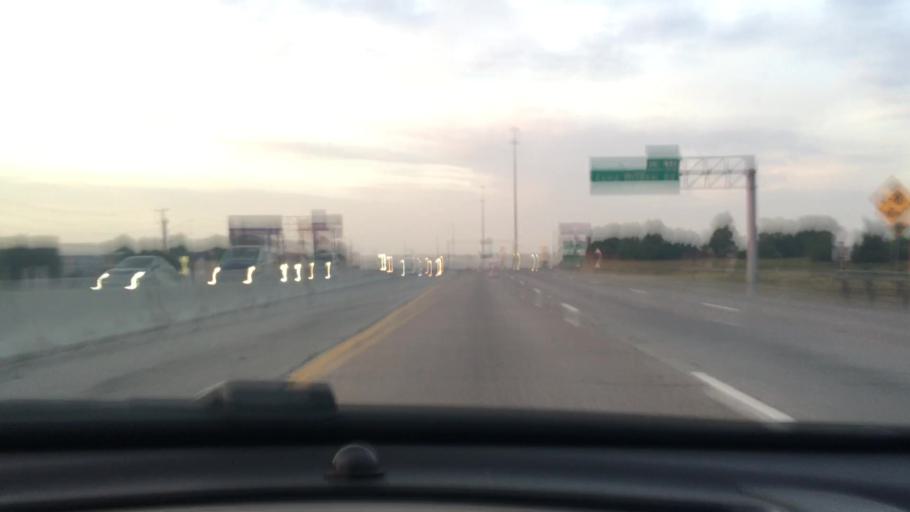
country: US
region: Texas
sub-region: Dallas County
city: DeSoto
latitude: 32.6691
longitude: -96.8227
